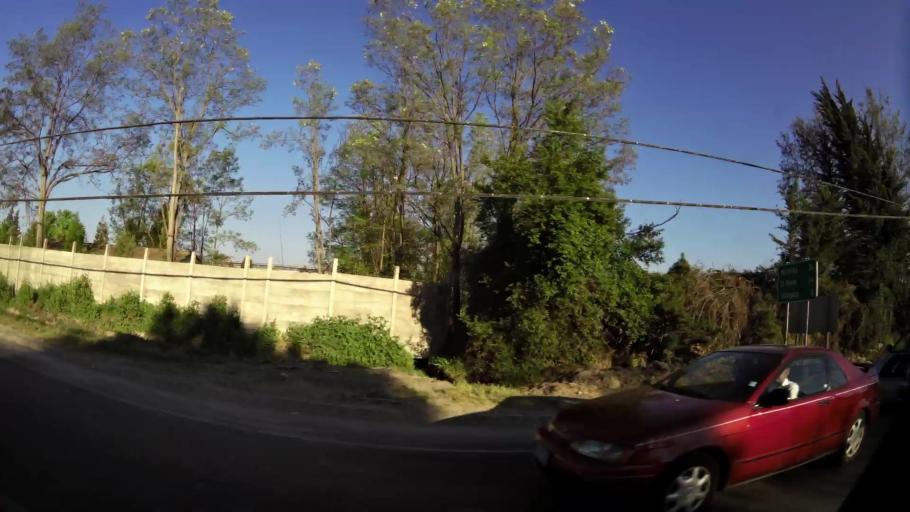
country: CL
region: Santiago Metropolitan
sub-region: Provincia de Talagante
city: Penaflor
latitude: -33.6115
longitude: -70.8588
